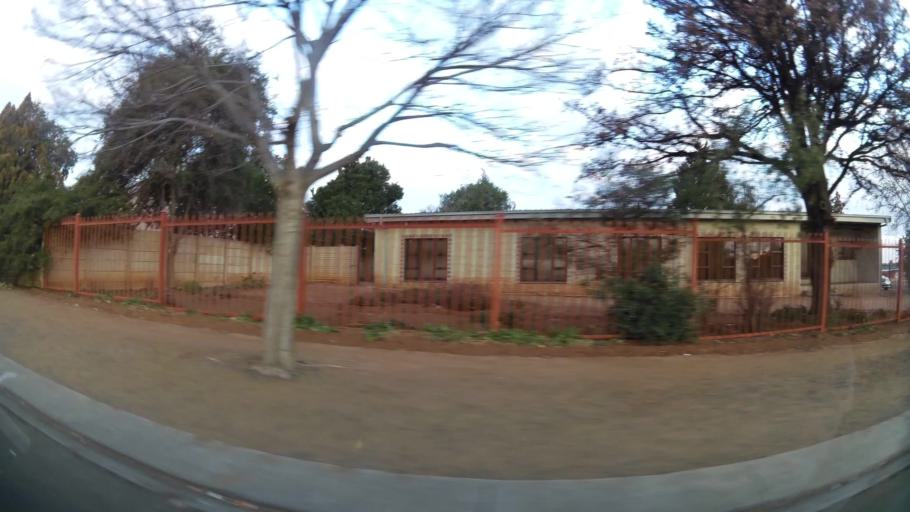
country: ZA
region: Orange Free State
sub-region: Mangaung Metropolitan Municipality
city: Bloemfontein
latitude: -29.1604
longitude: 26.1891
